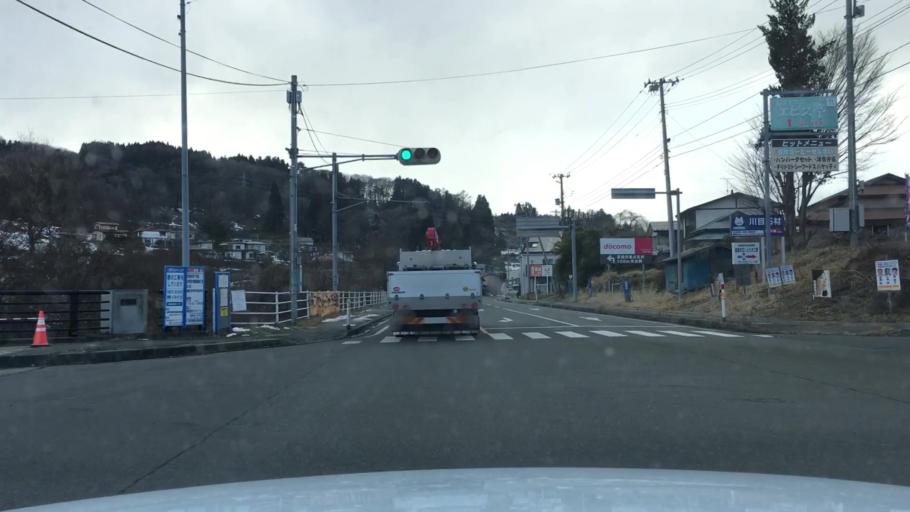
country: JP
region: Iwate
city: Morioka-shi
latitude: 39.6805
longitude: 141.1856
